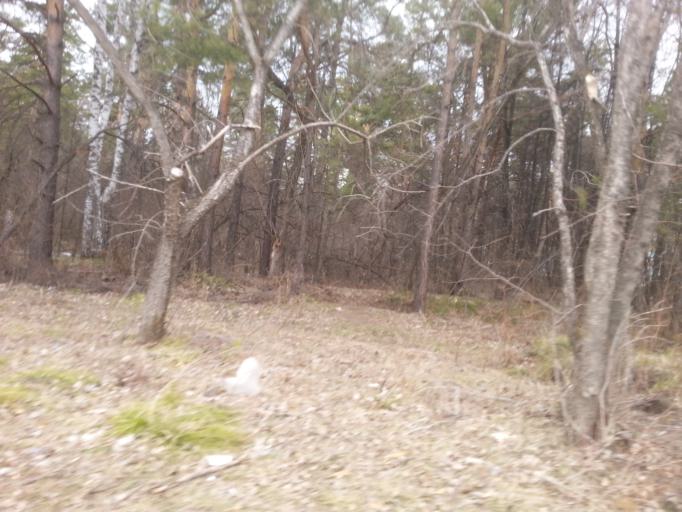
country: RU
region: Altai Krai
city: Zaton
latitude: 53.2854
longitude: 83.7524
